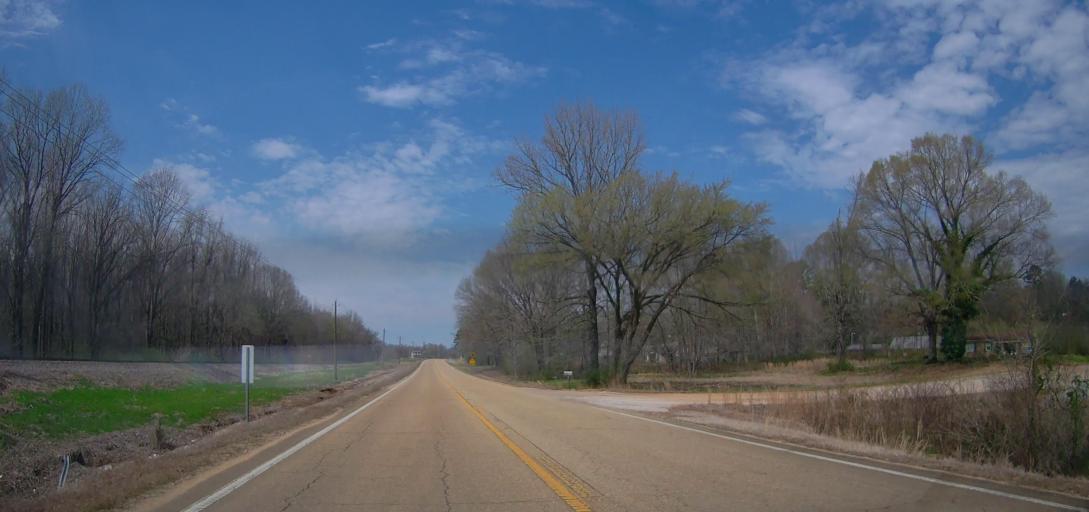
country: US
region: Mississippi
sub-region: Benton County
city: Ashland
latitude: 34.6292
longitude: -89.2675
